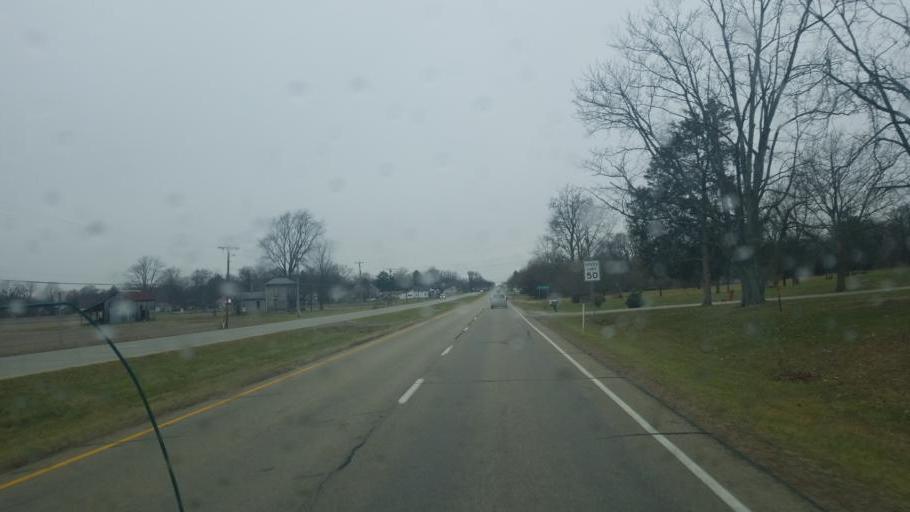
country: US
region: Indiana
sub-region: Henry County
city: Knightstown
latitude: 39.7916
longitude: -85.6063
